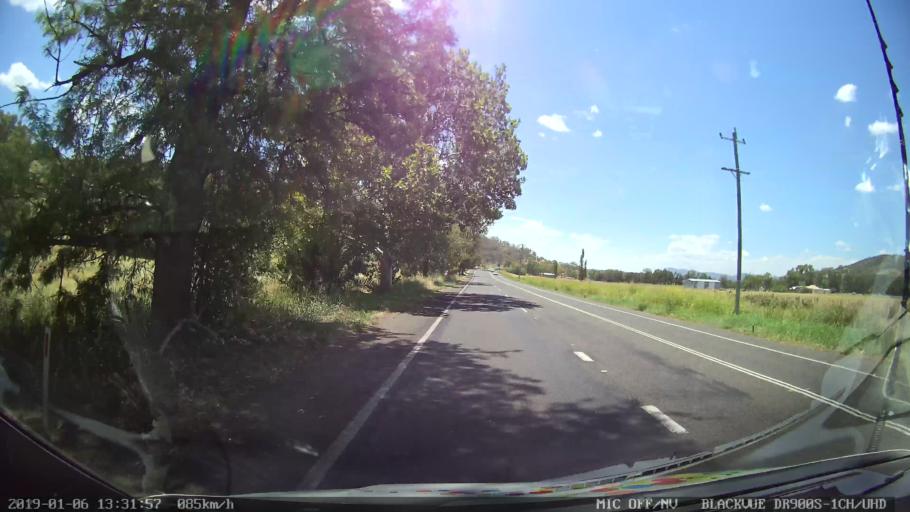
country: AU
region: New South Wales
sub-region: Tamworth Municipality
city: East Tamworth
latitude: -31.1157
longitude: 150.9962
